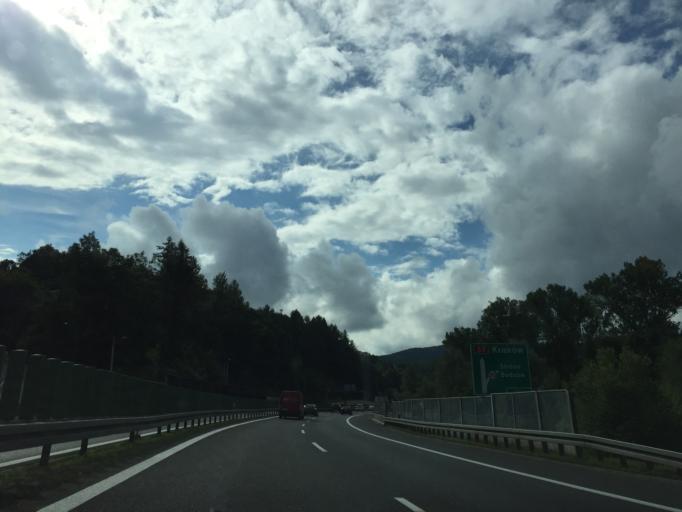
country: PL
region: Lesser Poland Voivodeship
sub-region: Powiat myslenicki
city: Stroza
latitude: 49.7888
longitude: 19.9327
